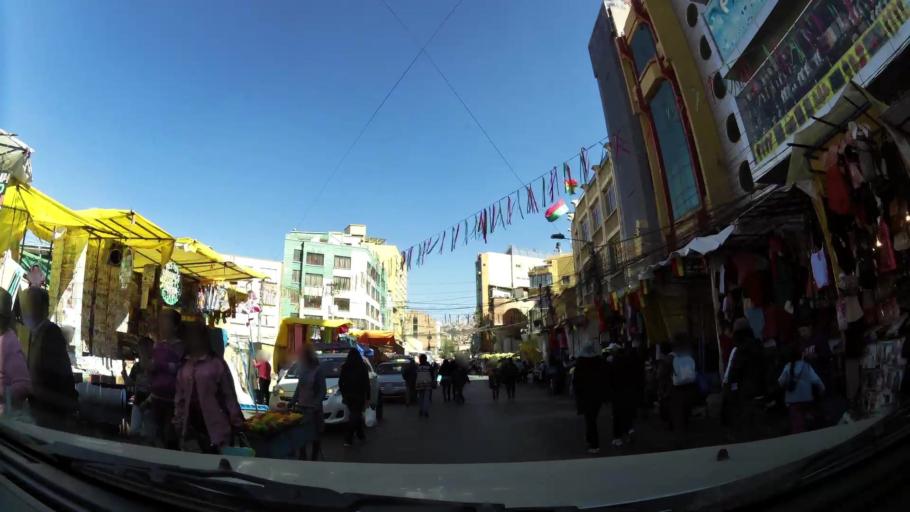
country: BO
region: La Paz
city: La Paz
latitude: -16.4942
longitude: -68.1441
